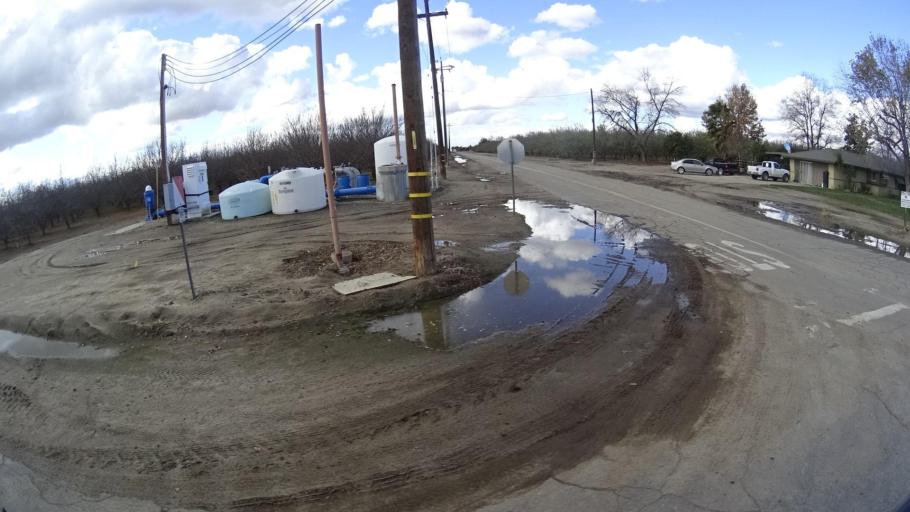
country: US
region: California
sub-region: Kern County
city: Greenfield
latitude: 35.2234
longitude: -119.0569
